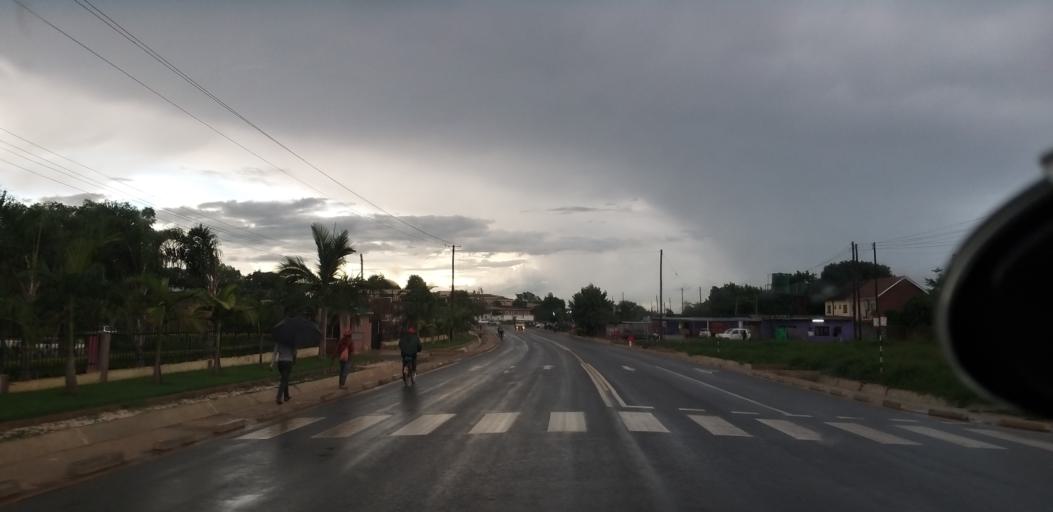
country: ZM
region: Lusaka
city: Lusaka
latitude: -15.4230
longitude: 28.3571
